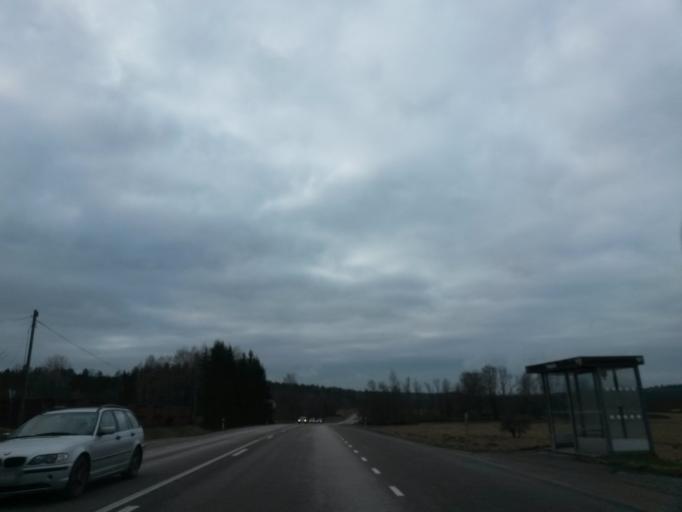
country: SE
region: Vaestra Goetaland
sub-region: Alingsas Kommun
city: Alingsas
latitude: 57.9404
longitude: 12.5874
